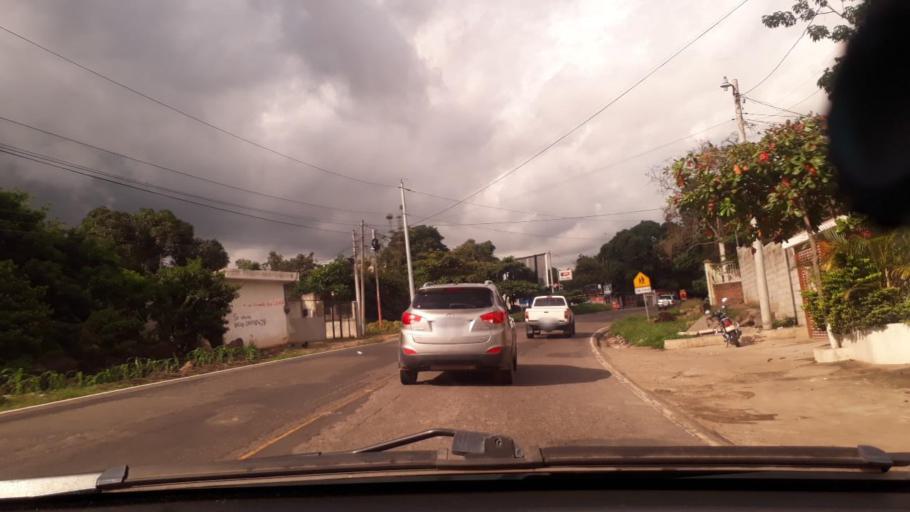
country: GT
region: Jutiapa
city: Quesada
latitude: 14.2748
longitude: -90.0035
